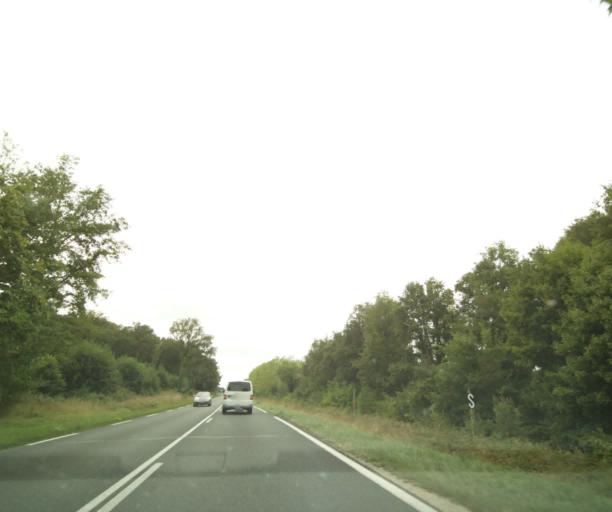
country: FR
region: Centre
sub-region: Departement d'Indre-et-Loire
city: Perrusson
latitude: 47.0731
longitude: 1.0705
